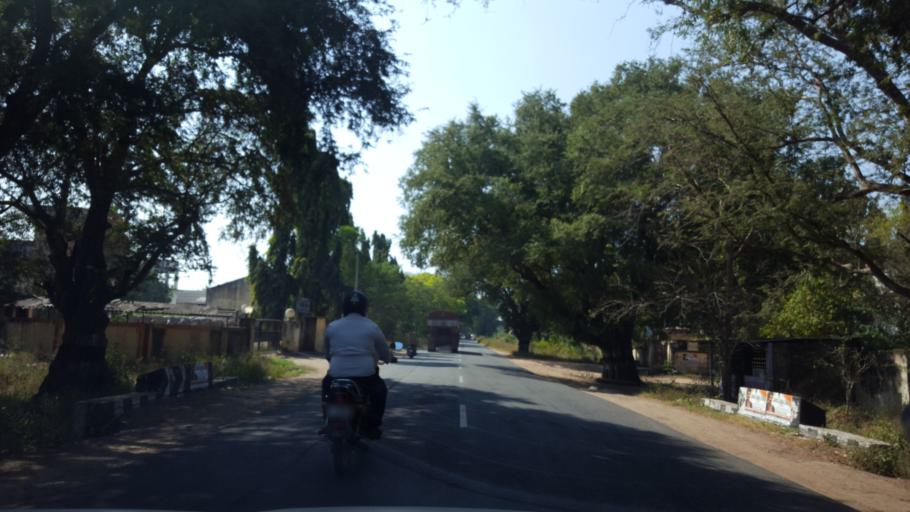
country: IN
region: Tamil Nadu
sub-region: Kancheepuram
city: Kanchipuram
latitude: 12.8622
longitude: 79.6698
